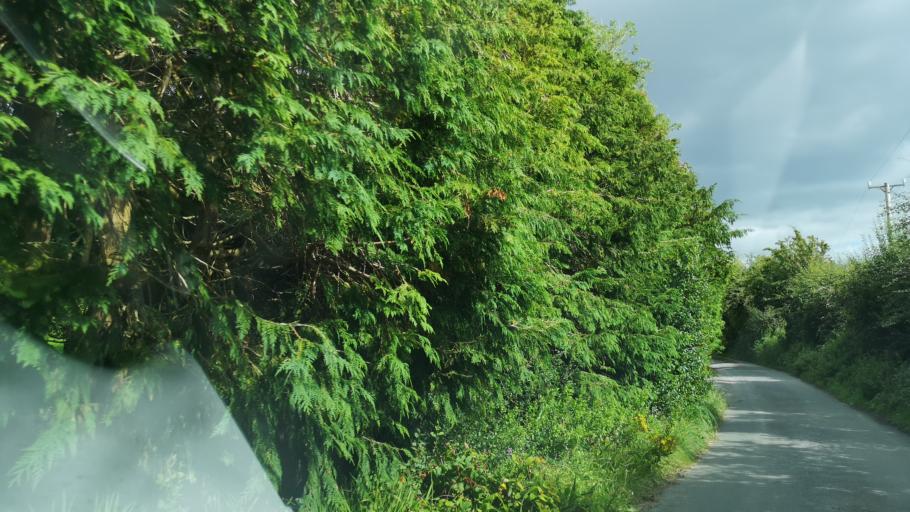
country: IE
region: Connaught
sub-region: County Galway
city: Moycullen
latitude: 53.3202
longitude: -9.1425
